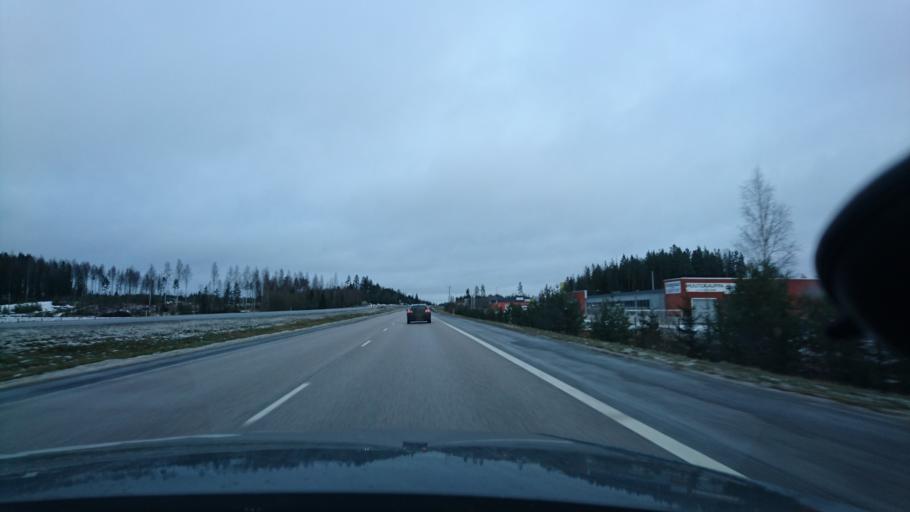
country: FI
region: Uusimaa
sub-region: Helsinki
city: Maentsaelae
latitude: 60.6167
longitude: 25.2729
